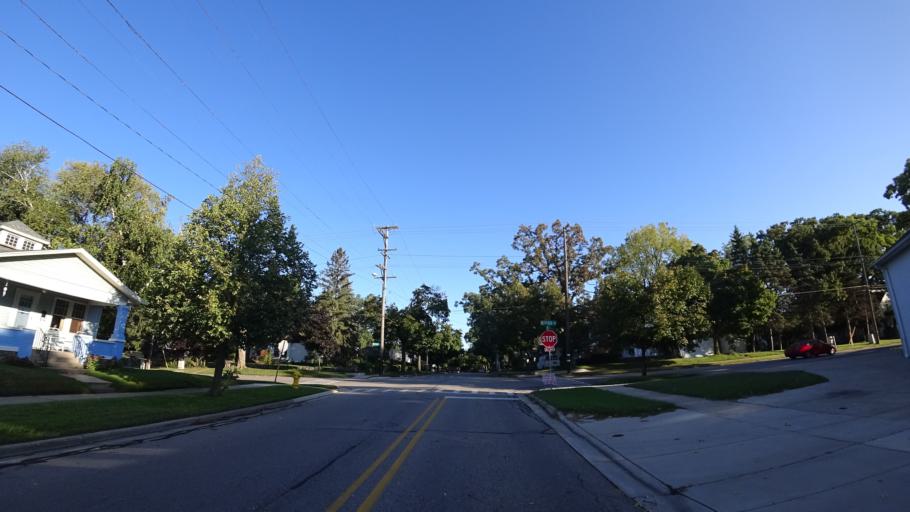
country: US
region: Michigan
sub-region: Kent County
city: Grand Rapids
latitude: 42.9988
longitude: -85.6646
